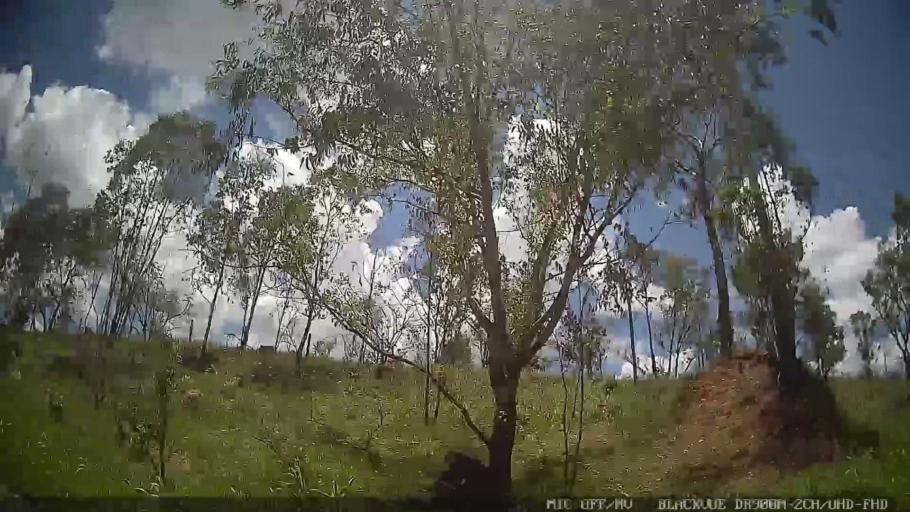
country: BR
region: Sao Paulo
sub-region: Amparo
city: Amparo
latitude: -22.6504
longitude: -46.7419
